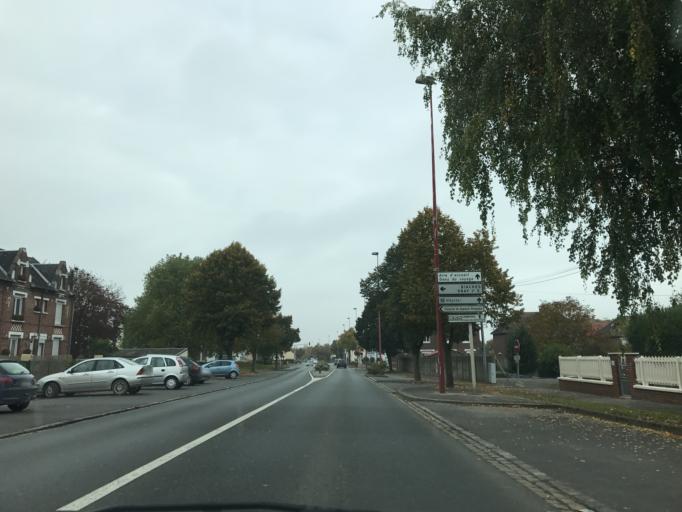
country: FR
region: Picardie
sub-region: Departement de la Somme
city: Peronne
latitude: 49.9108
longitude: 2.9327
